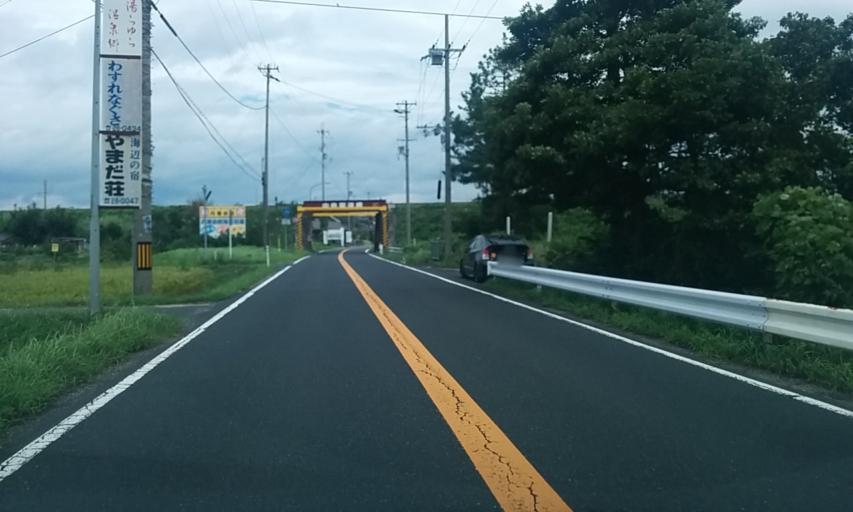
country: JP
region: Kyoto
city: Maizuru
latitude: 35.5115
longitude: 135.2846
